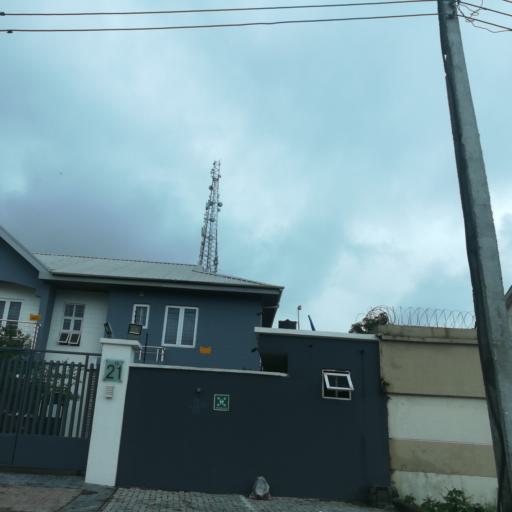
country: NG
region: Lagos
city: Ikoyi
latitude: 6.4407
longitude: 3.4638
